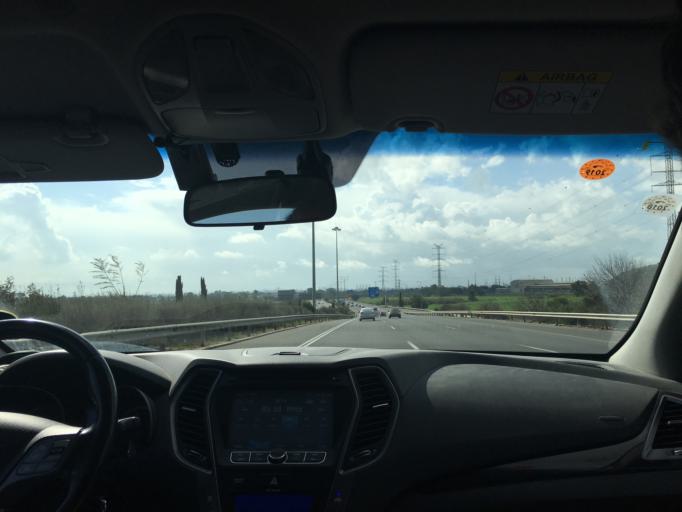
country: IL
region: Tel Aviv
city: Azor
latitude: 32.0372
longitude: 34.8297
